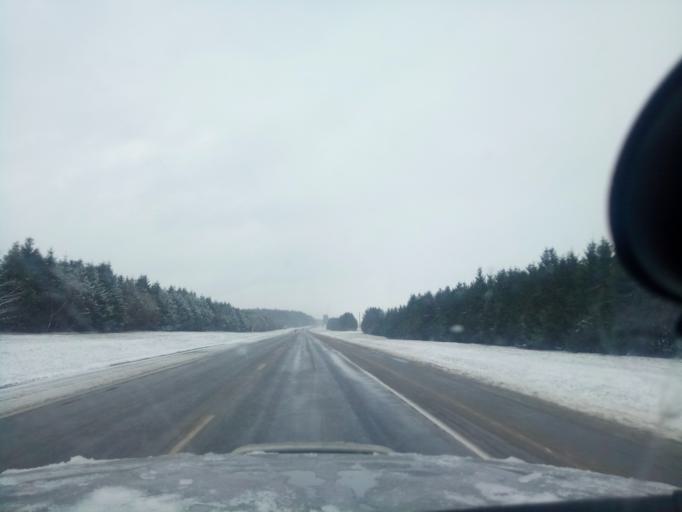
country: BY
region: Minsk
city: Haradzyeya
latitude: 53.2892
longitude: 26.5805
